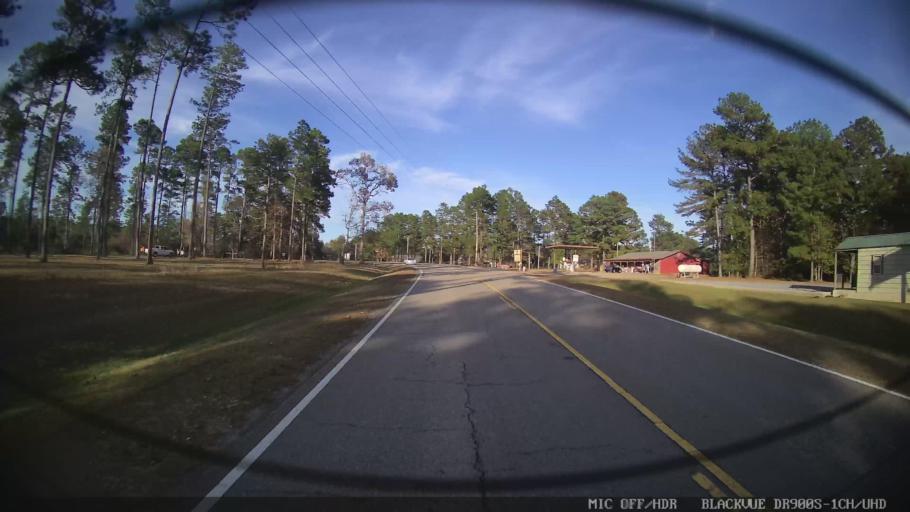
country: US
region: Mississippi
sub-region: Lamar County
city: Purvis
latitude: 31.1900
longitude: -89.2879
